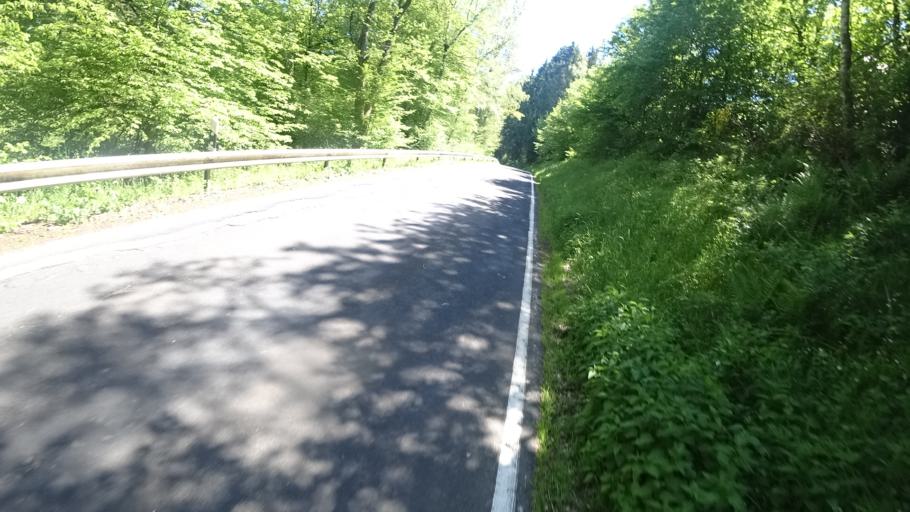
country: DE
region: Rheinland-Pfalz
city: Elben
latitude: 50.7485
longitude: 7.8375
